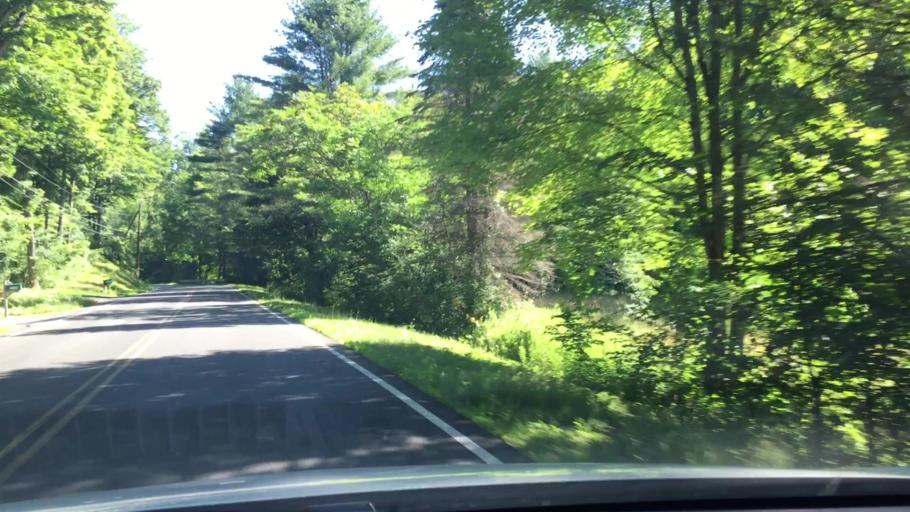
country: US
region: Massachusetts
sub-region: Berkshire County
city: West Stockbridge
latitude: 42.3565
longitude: -73.3550
